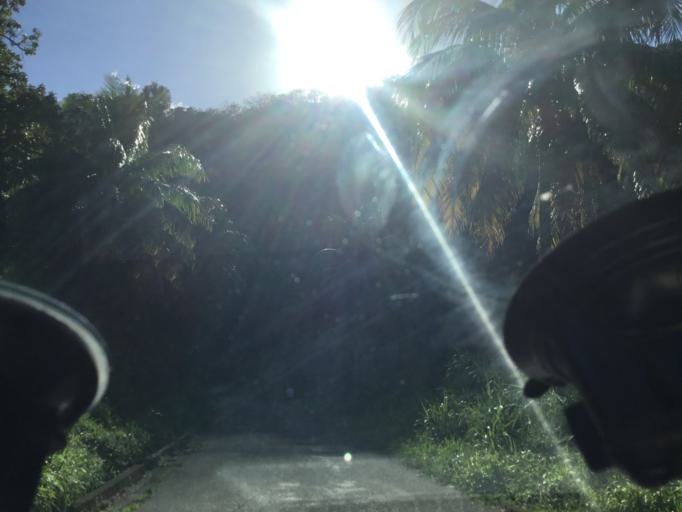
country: VC
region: Saint David
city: Chateaubelair
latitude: 13.2994
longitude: -61.2286
